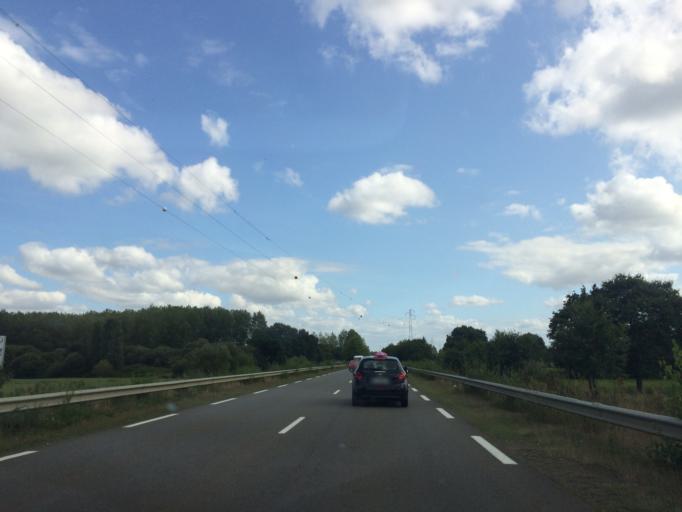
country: FR
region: Brittany
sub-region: Departement d'Ille-et-Vilaine
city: Chavagne
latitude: 48.0753
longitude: -1.7912
